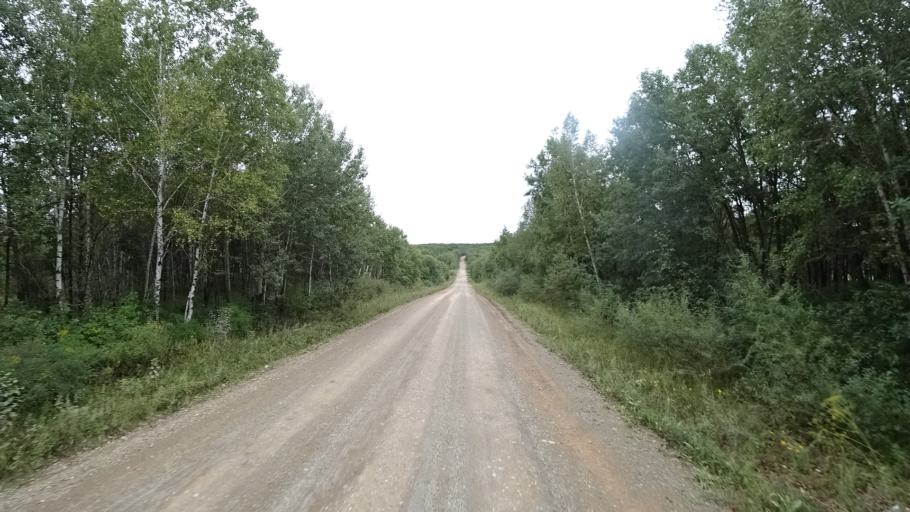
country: RU
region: Primorskiy
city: Ivanovka
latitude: 44.0305
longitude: 132.5088
